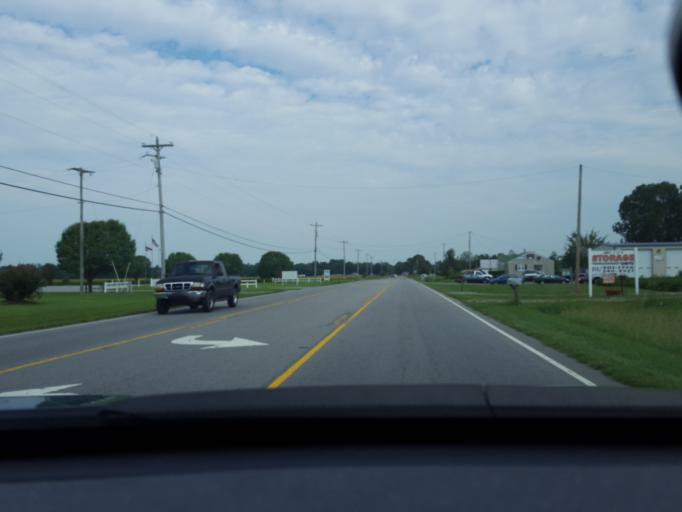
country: US
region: North Carolina
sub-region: Chowan County
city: Edenton
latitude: 36.0898
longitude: -76.6295
